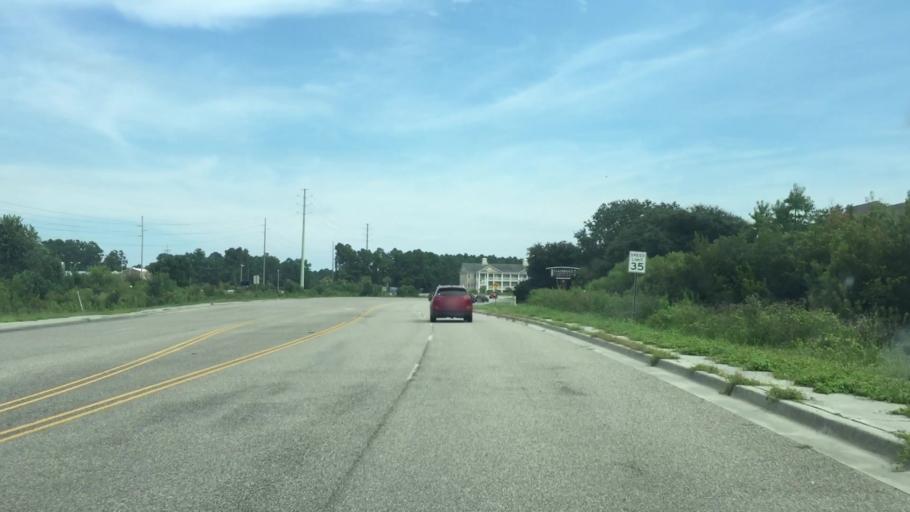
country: US
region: South Carolina
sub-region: Horry County
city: Forestbrook
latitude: 33.7148
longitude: -78.9293
